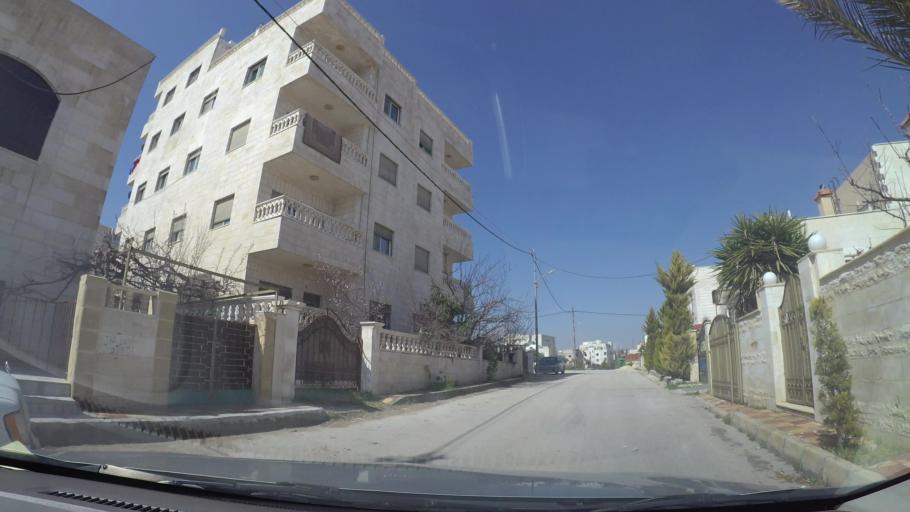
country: JO
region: Amman
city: Al Bunayyat ash Shamaliyah
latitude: 31.8926
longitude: 35.8964
